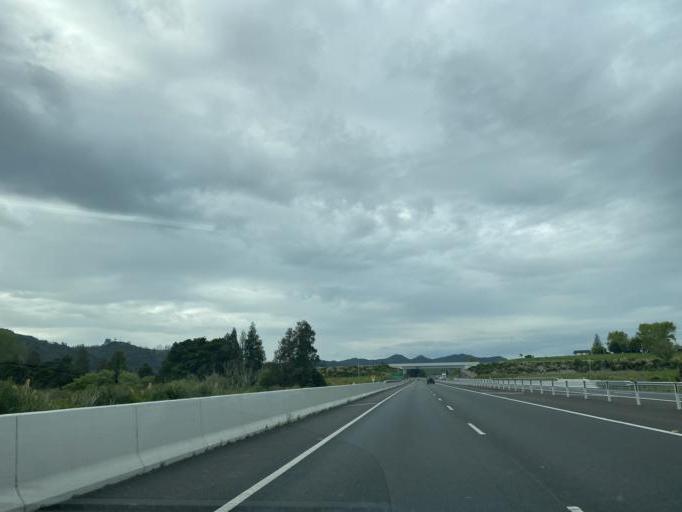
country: NZ
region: Waikato
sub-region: Waikato District
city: Ngaruawahia
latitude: -37.6150
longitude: 175.2048
